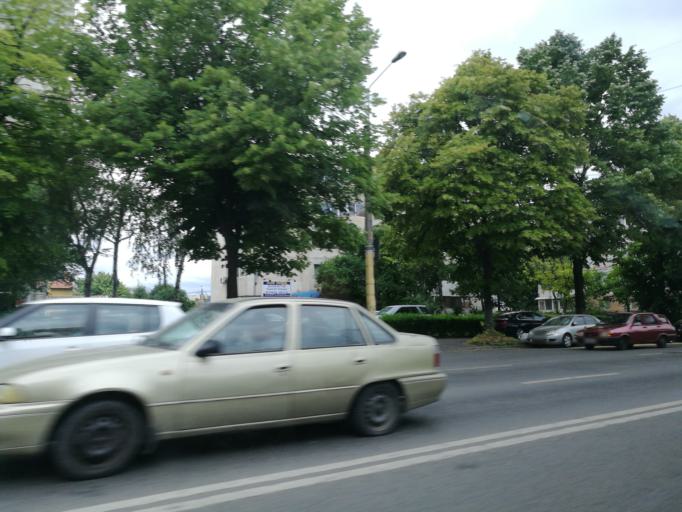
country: RO
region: Constanta
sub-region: Municipiul Constanta
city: Constanta
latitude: 44.1894
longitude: 28.6338
